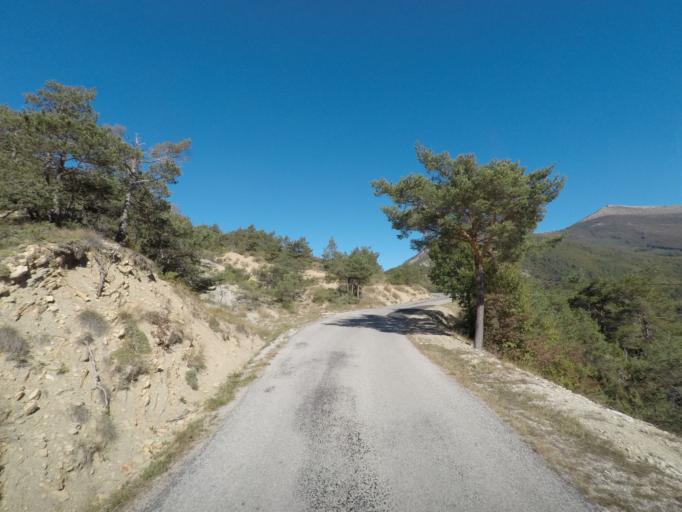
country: FR
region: Rhone-Alpes
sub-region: Departement de la Drome
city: Die
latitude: 44.5576
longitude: 5.3226
